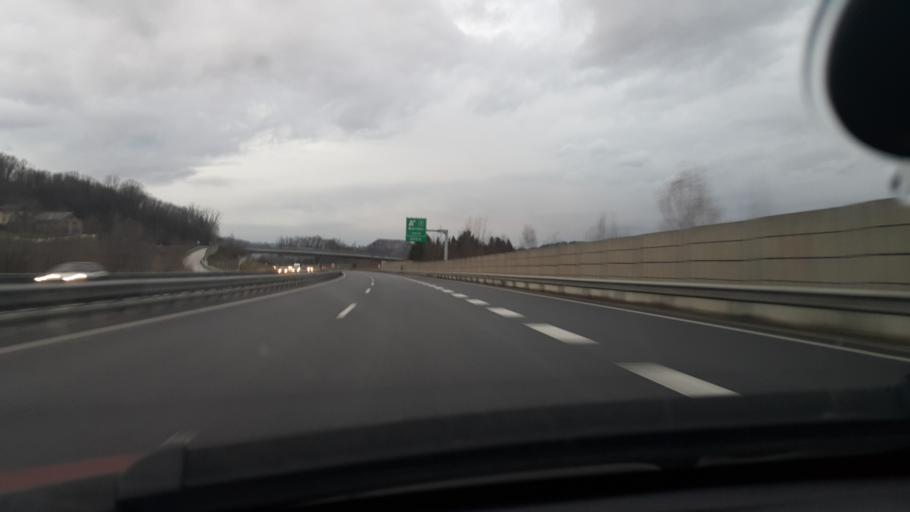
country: SI
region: Pesnica
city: Pesnica pri Mariboru
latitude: 46.5900
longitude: 15.6841
